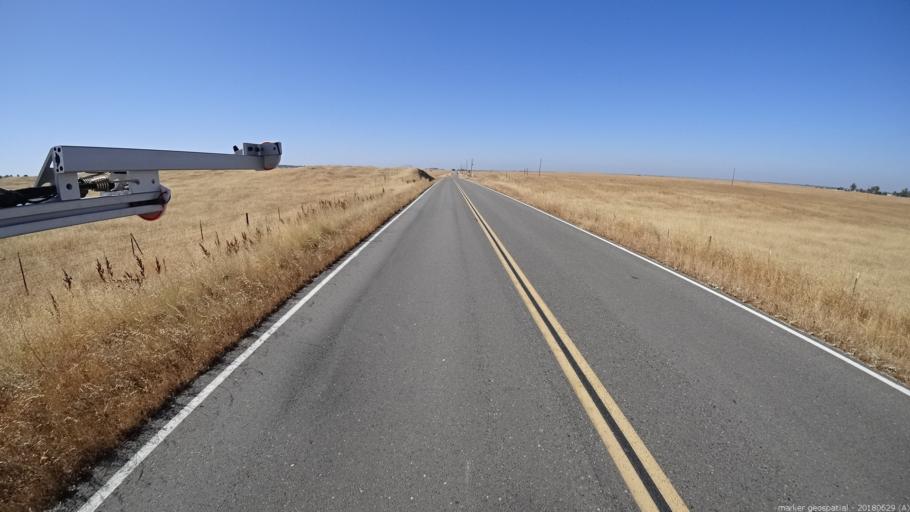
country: US
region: California
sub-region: Madera County
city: Bonadelle Ranchos-Madera Ranchos
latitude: 37.0411
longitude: -119.7937
